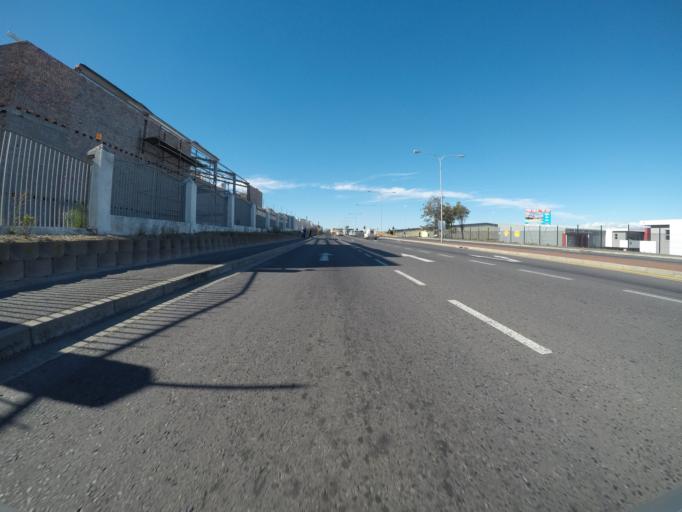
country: ZA
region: Western Cape
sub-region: City of Cape Town
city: Kraaifontein
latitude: -33.9071
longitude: 18.6668
